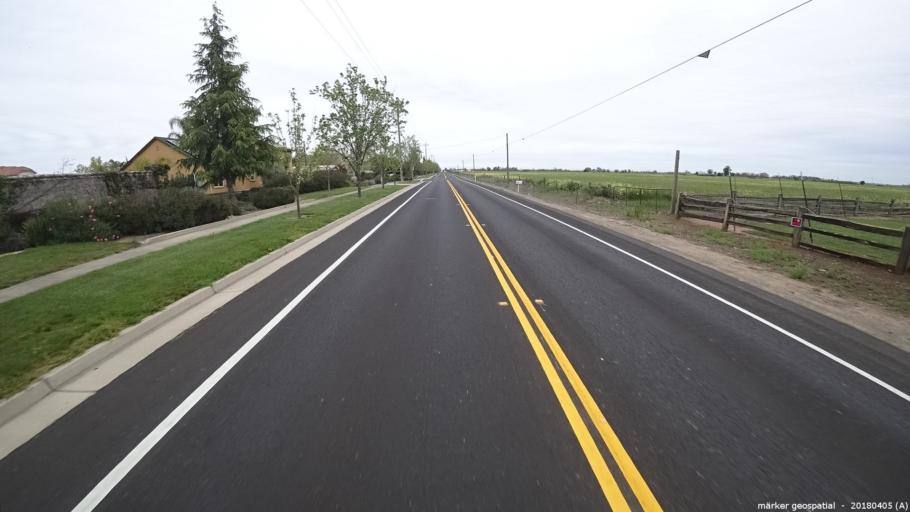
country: US
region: California
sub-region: Sacramento County
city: Laguna
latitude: 38.3793
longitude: -121.4397
